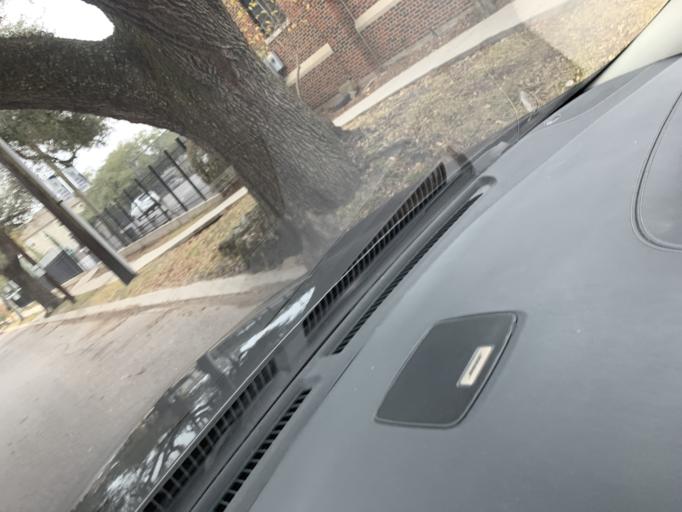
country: US
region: Louisiana
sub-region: Jefferson Parish
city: Metairie
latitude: 30.0058
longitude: -90.1067
